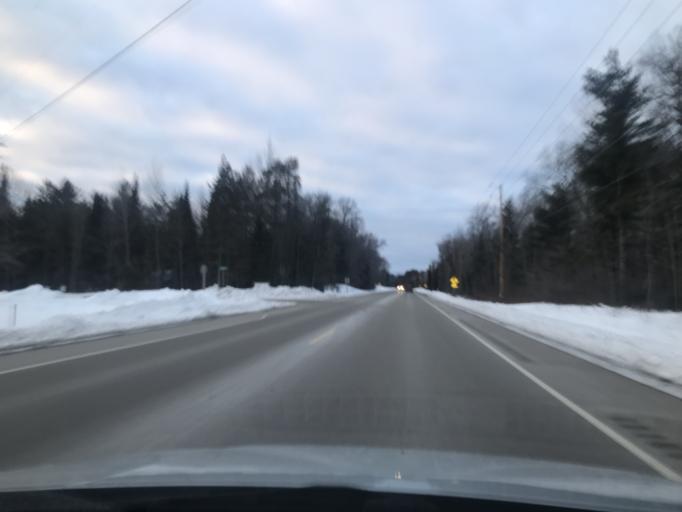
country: US
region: Wisconsin
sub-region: Marinette County
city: Peshtigo
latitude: 45.1640
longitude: -87.7262
